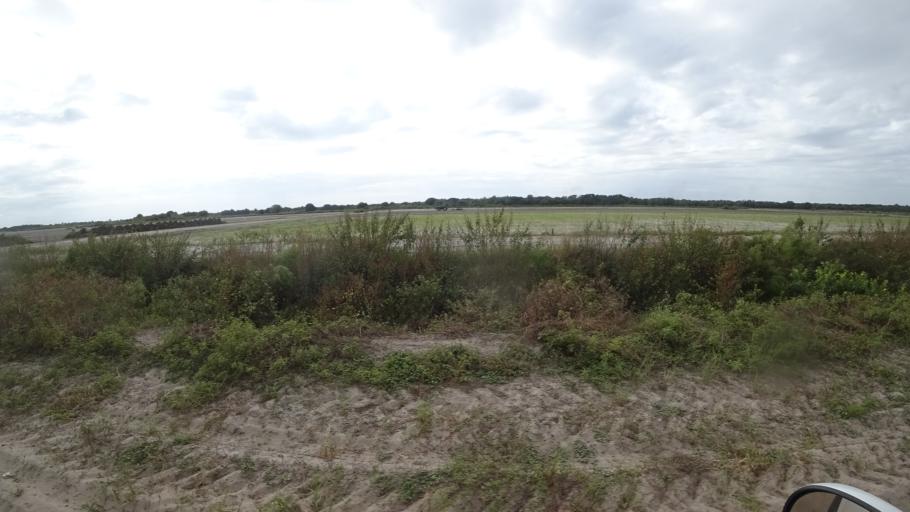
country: US
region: Florida
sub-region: Hillsborough County
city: Wimauma
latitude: 27.5625
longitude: -82.3000
